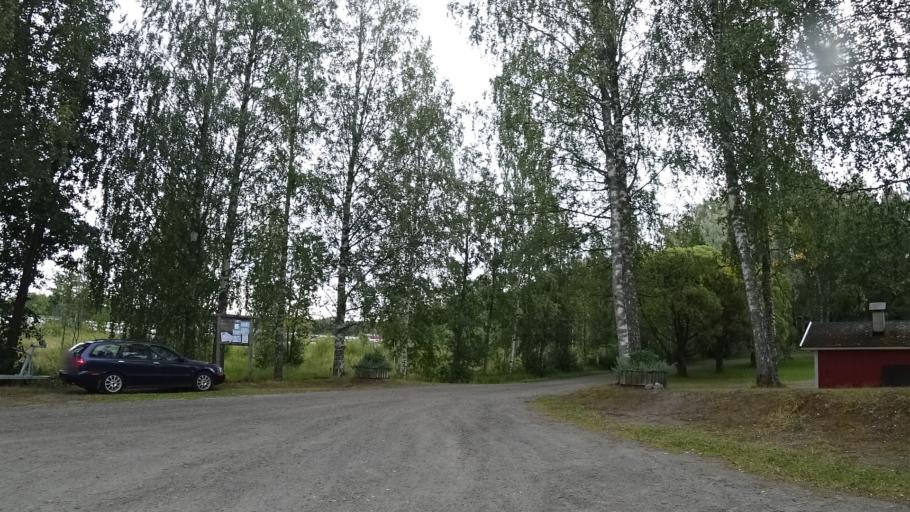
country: FI
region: North Karelia
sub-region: Keski-Karjala
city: Kesaelahti
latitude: 62.0962
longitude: 29.8749
